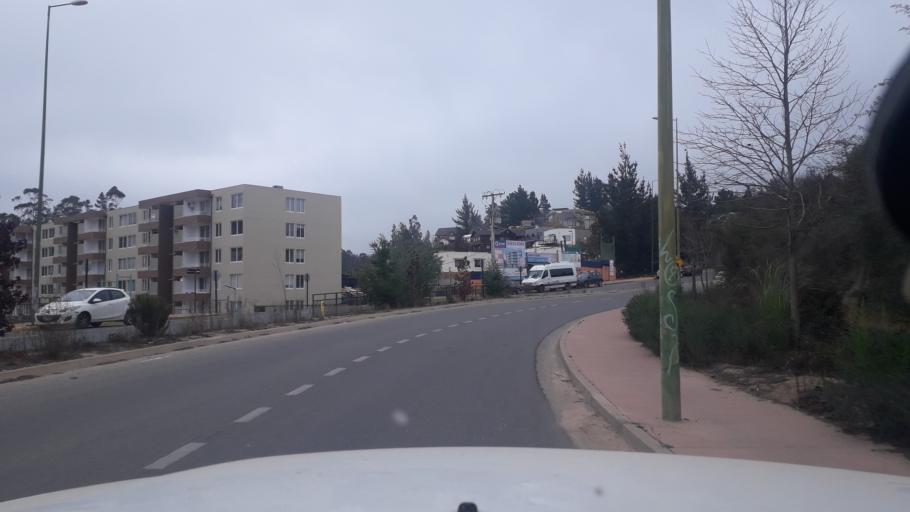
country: CL
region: Valparaiso
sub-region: Provincia de Valparaiso
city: Valparaiso
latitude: -33.1348
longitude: -71.5722
